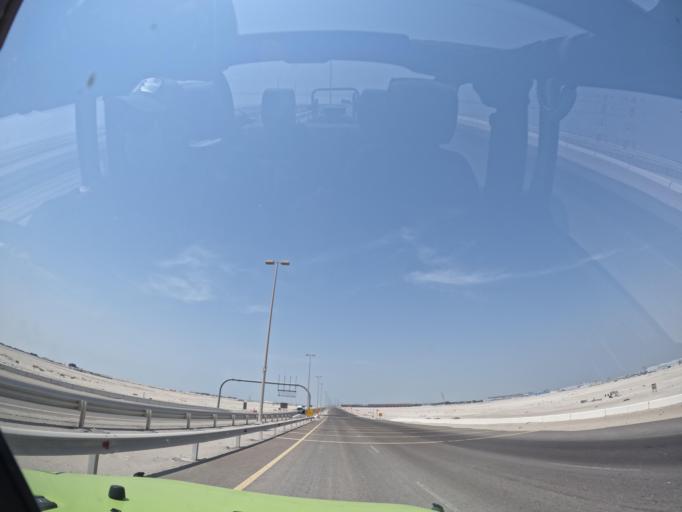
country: AE
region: Abu Dhabi
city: Abu Dhabi
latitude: 24.2561
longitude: 54.4634
